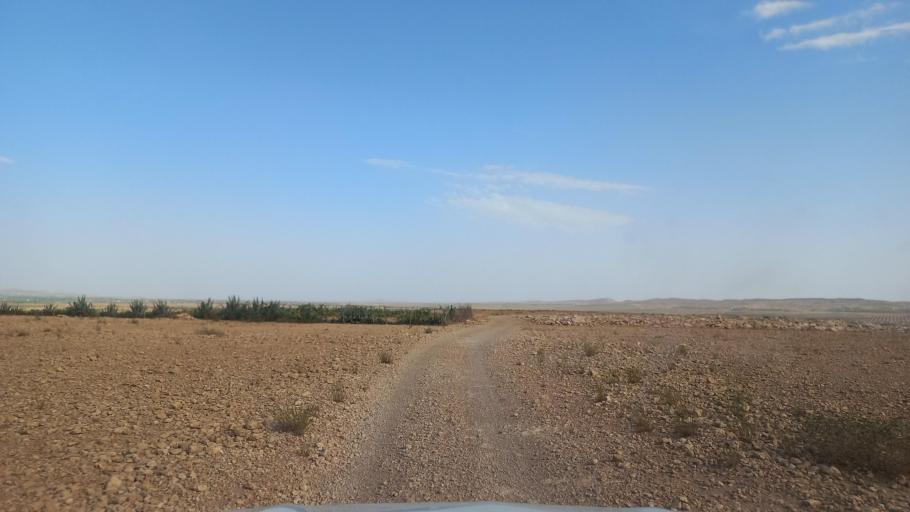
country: TN
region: Al Qasrayn
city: Kasserine
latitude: 35.2585
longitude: 8.9309
